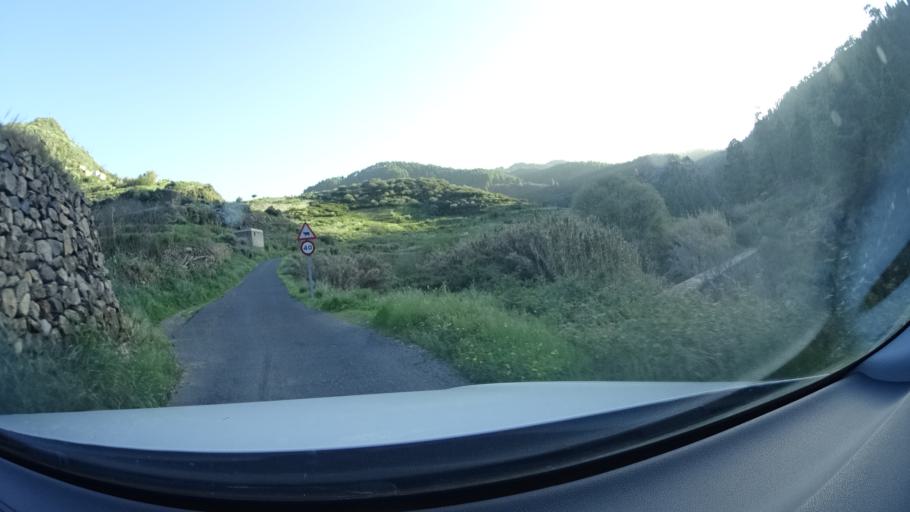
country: ES
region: Canary Islands
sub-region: Provincia de Las Palmas
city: Artenara
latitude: 28.0415
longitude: -15.6755
